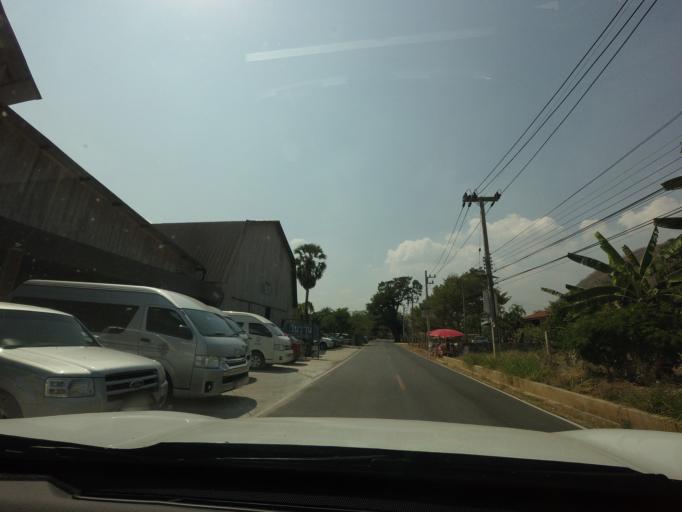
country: TH
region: Nakhon Ratchasima
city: Pak Chong
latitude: 14.5834
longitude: 101.4382
